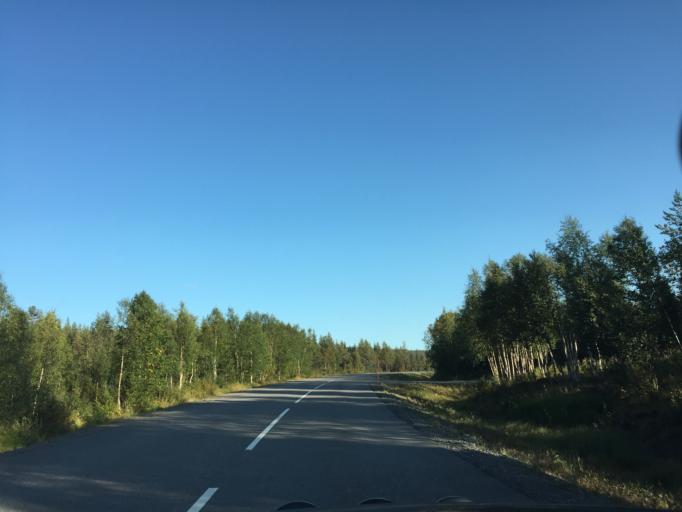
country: SE
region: Norrbotten
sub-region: Gallivare Kommun
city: Malmberget
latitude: 67.6388
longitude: 21.0686
